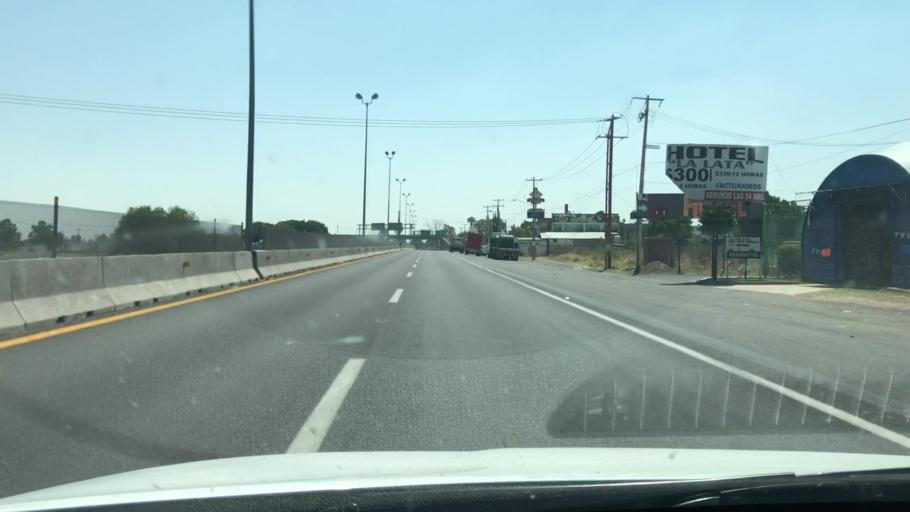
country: MX
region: Guanajuato
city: Abasolo
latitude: 20.4651
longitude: -101.5135
